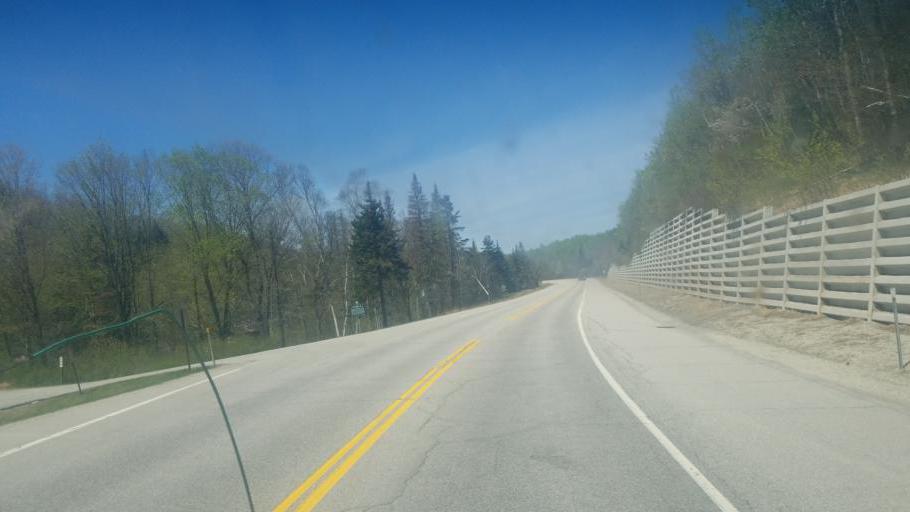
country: US
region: New Hampshire
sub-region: Grafton County
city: Deerfield
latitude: 44.2653
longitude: -71.4987
